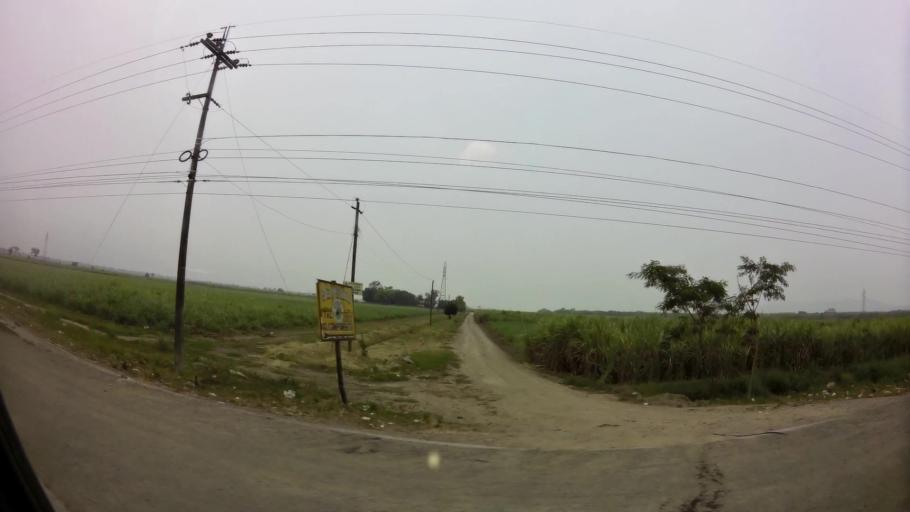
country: HN
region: Cortes
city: La Lima
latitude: 15.4116
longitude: -87.8635
